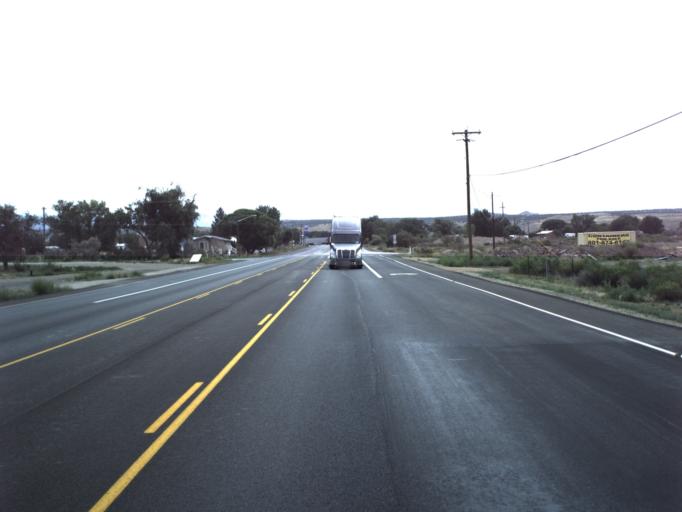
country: US
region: Utah
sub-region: Carbon County
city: Wellington
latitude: 39.5425
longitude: -110.6950
